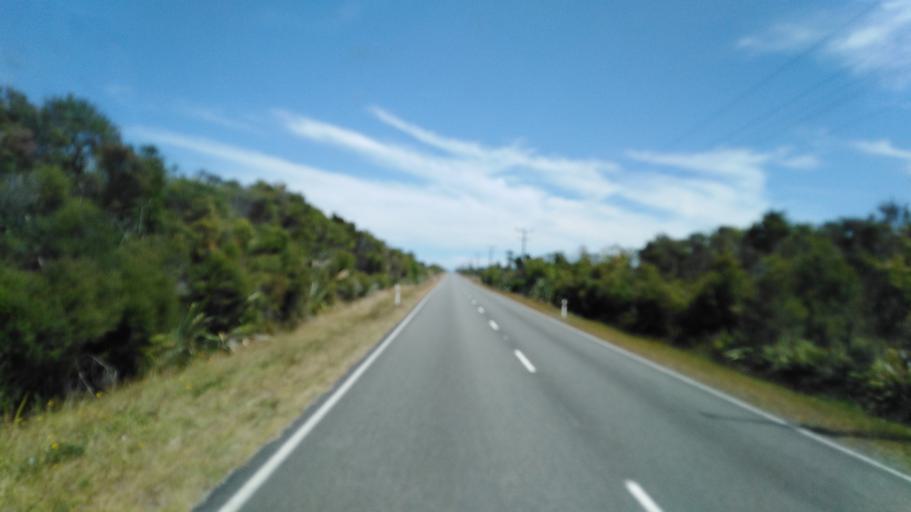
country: NZ
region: West Coast
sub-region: Buller District
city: Westport
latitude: -41.7461
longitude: 171.6837
